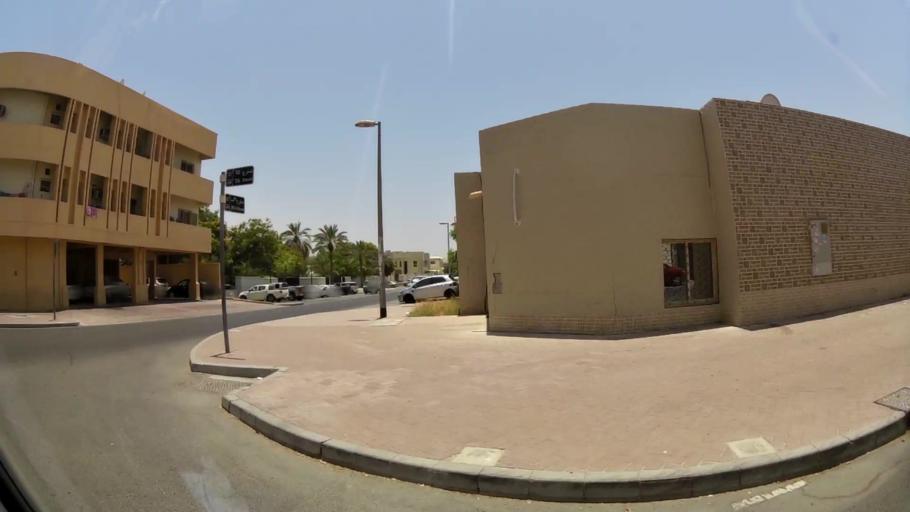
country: AE
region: Ash Shariqah
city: Sharjah
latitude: 25.2863
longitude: 55.3327
